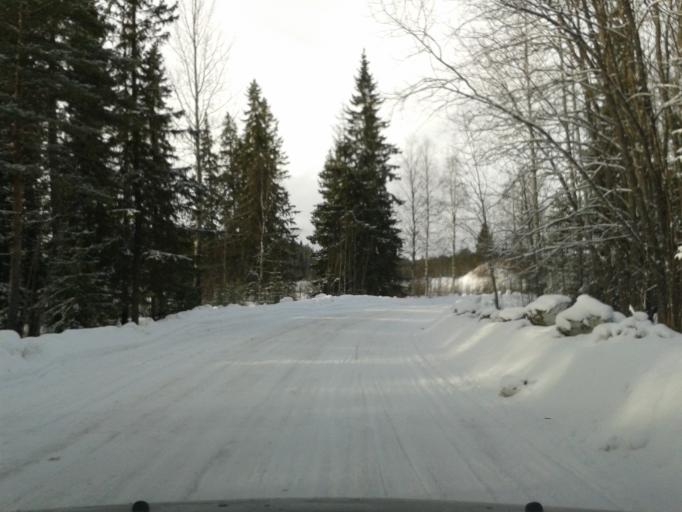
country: SE
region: Vaesterbotten
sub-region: Vilhelmina Kommun
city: Vilhelmina
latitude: 64.6176
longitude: 16.6558
